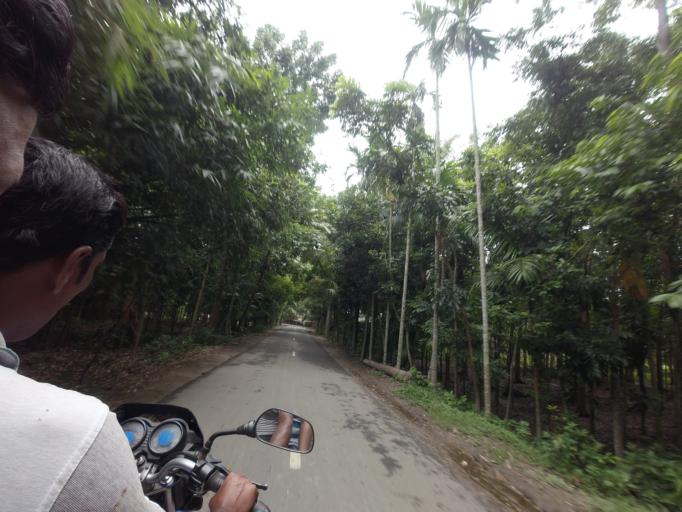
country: BD
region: Khulna
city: Kalia
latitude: 23.1174
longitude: 89.6477
